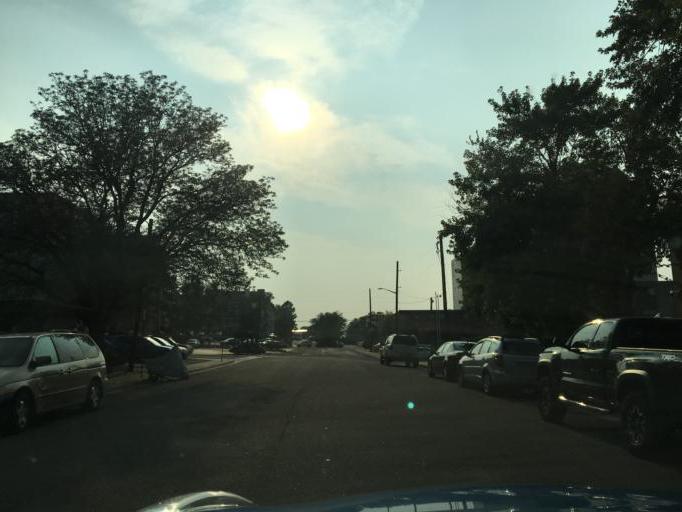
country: US
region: Colorado
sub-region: Arapahoe County
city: Glendale
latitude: 39.6948
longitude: -104.9354
